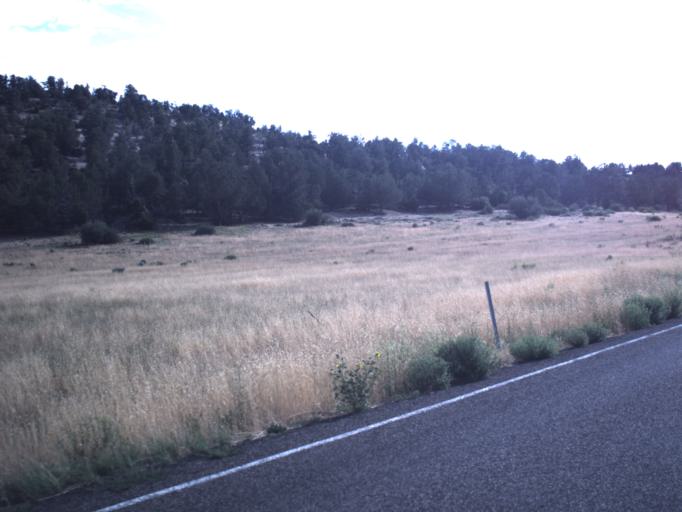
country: US
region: Utah
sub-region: Washington County
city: Hildale
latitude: 37.2402
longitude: -112.8264
